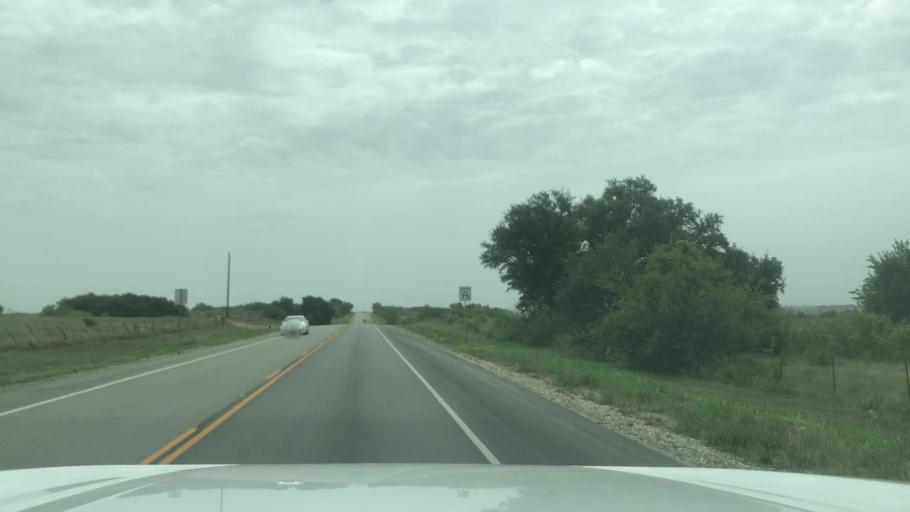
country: US
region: Texas
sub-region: Erath County
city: Dublin
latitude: 32.0834
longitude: -98.2496
